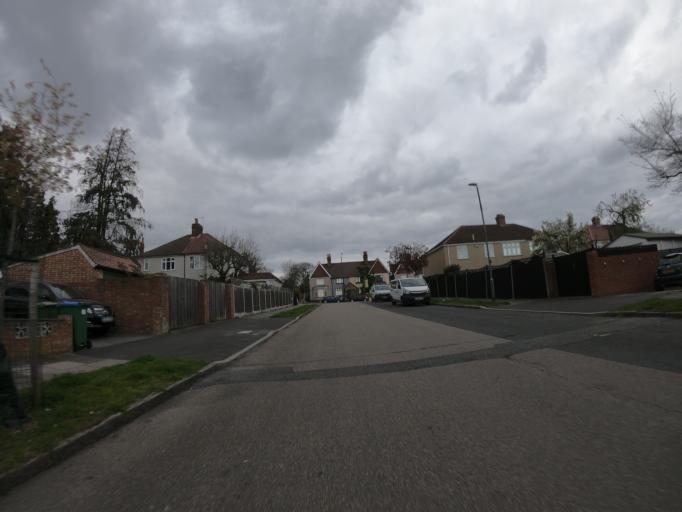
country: GB
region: England
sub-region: Greater London
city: Bexleyheath
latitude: 51.4781
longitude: 0.1383
